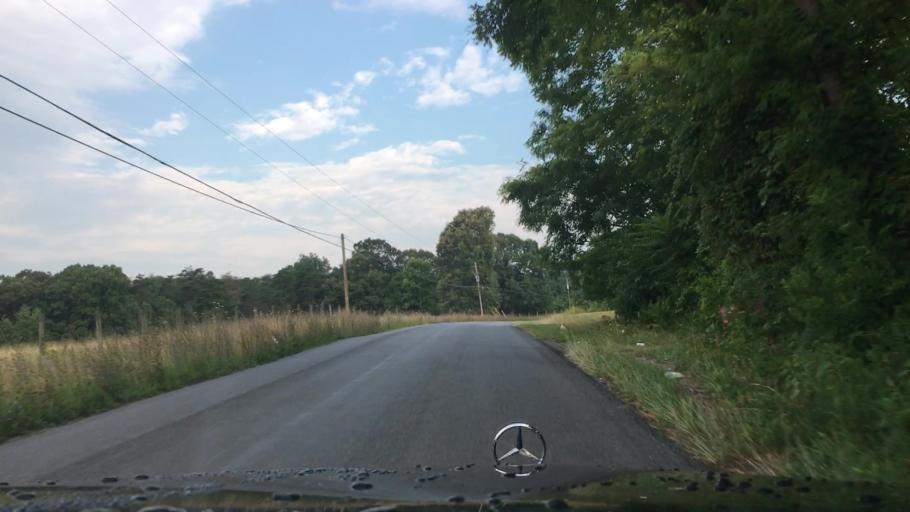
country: US
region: Virginia
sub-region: Campbell County
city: Altavista
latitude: 37.1462
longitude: -79.2899
